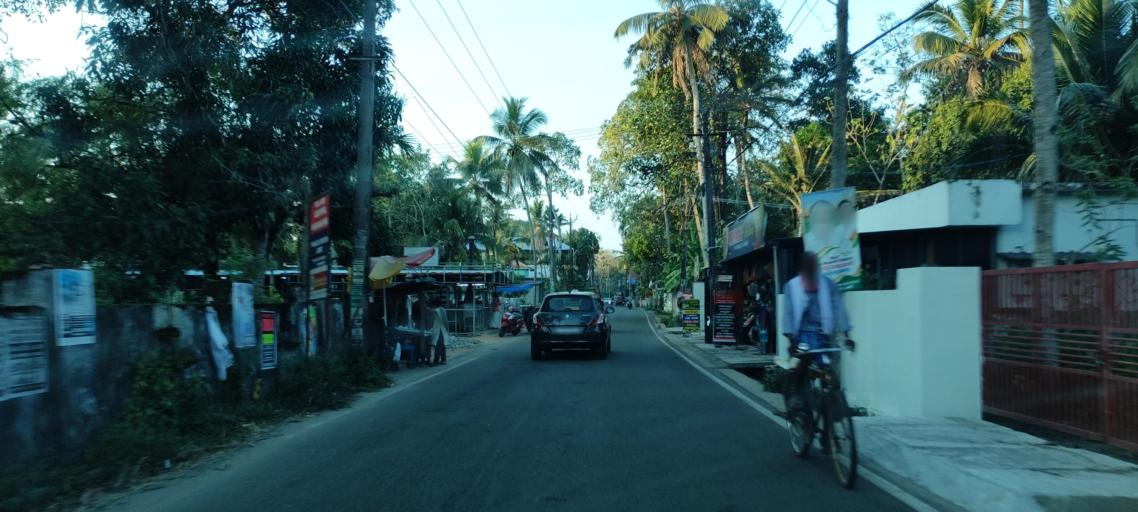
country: IN
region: Kerala
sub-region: Alappuzha
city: Kayankulam
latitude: 9.2358
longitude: 76.4558
